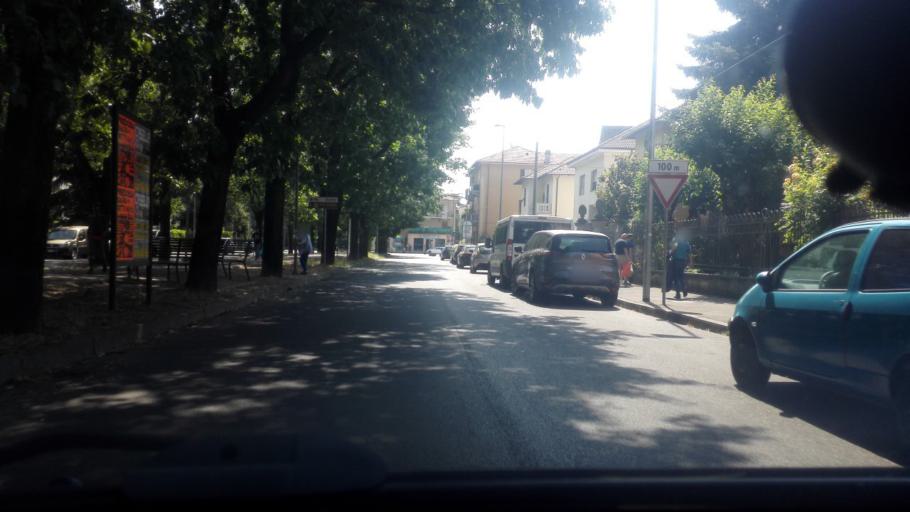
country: IT
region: Piedmont
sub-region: Provincia di Alessandria
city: Novi Ligure
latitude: 44.7659
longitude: 8.7959
